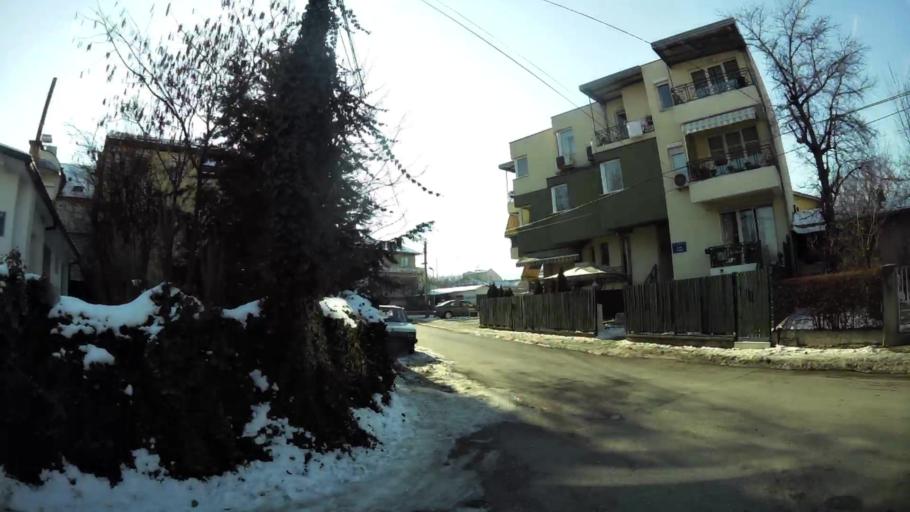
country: MK
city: Krushopek
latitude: 42.0005
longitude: 21.3807
